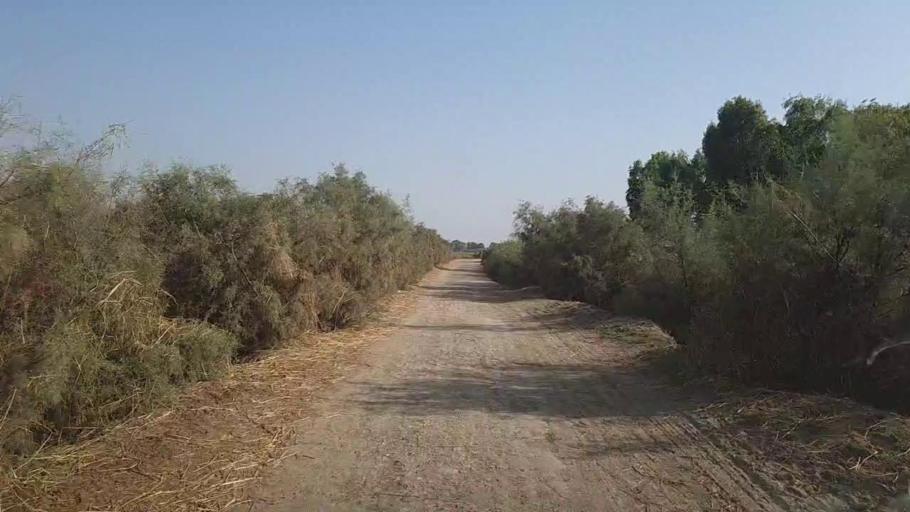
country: PK
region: Sindh
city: Kandhkot
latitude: 28.3560
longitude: 69.3346
